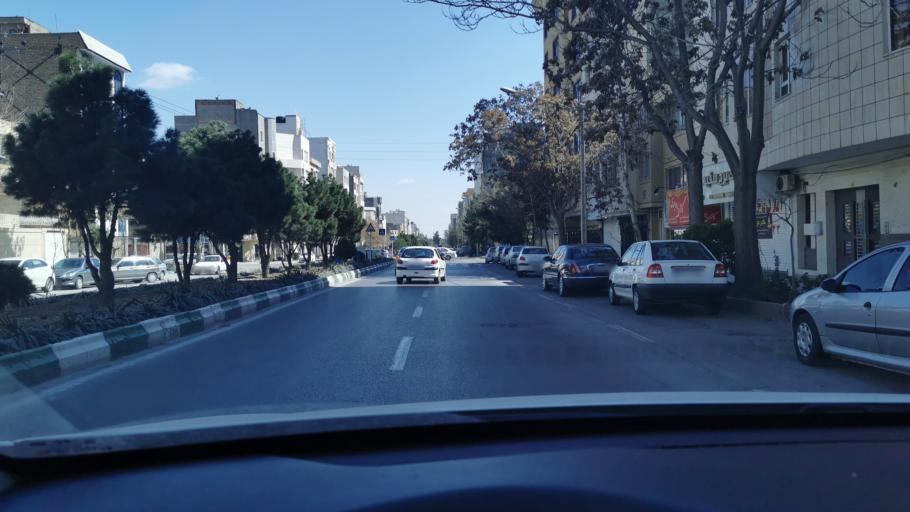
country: IR
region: Razavi Khorasan
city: Mashhad
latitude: 36.3256
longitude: 59.5224
